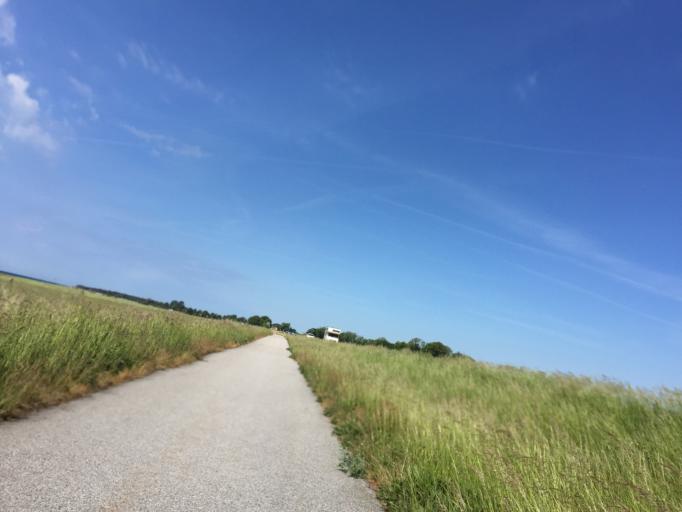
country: SE
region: Skane
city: Smygehamn
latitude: 55.3417
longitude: 13.3359
